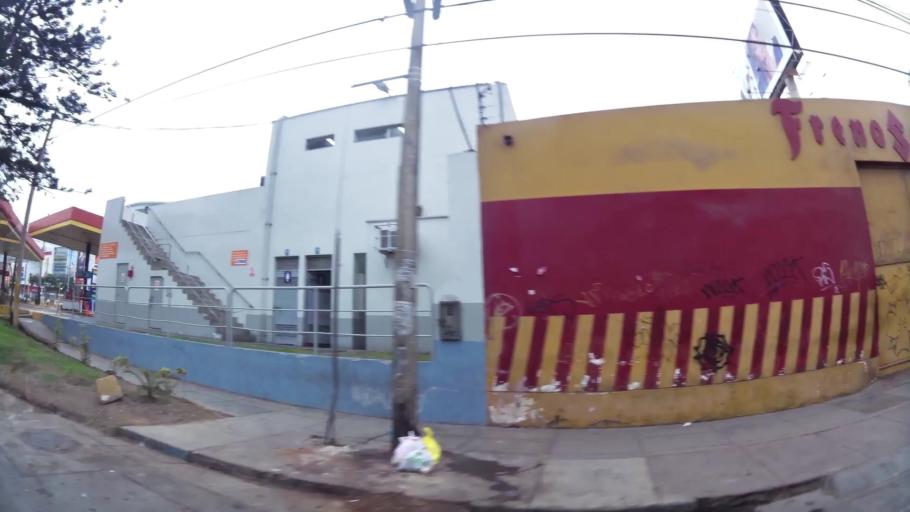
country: PE
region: Lima
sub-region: Lima
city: Surco
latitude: -12.1131
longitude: -77.0122
